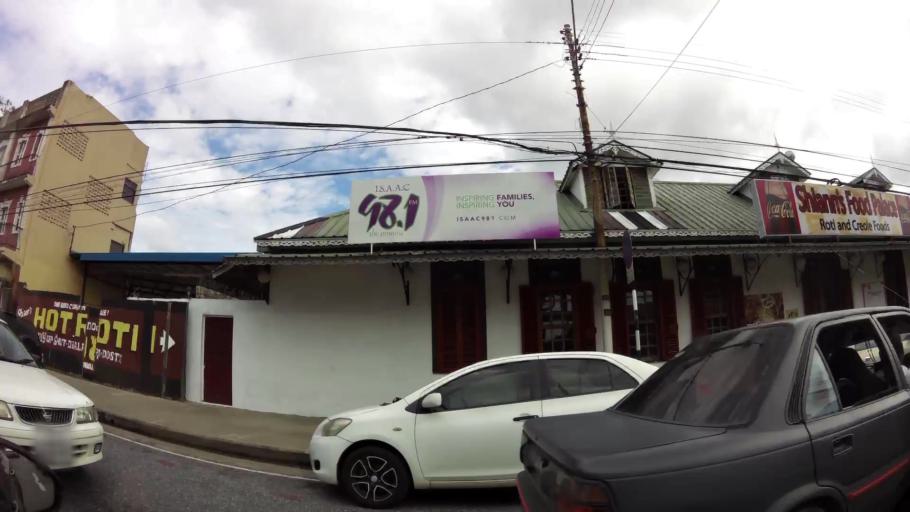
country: TT
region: City of Port of Spain
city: Port-of-Spain
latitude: 10.6612
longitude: -61.5179
